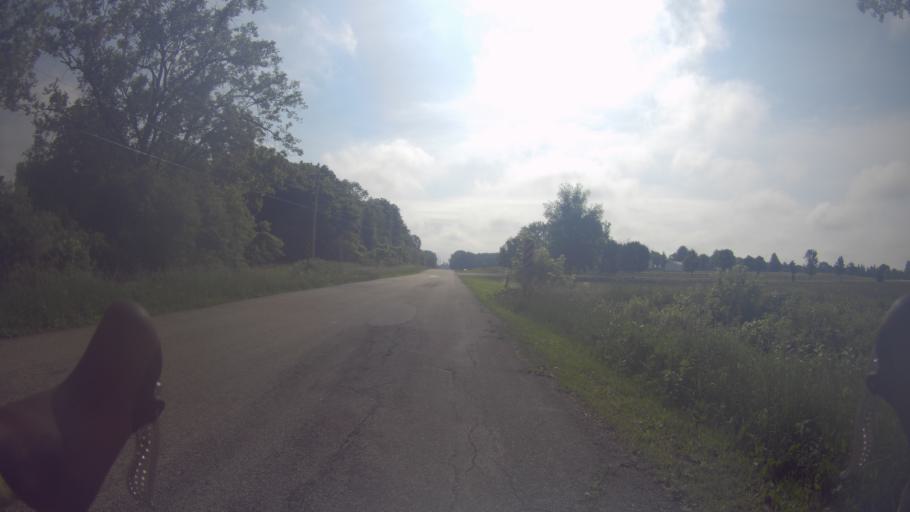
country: US
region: Wisconsin
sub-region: Dane County
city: McFarland
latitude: 42.9911
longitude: -89.2309
